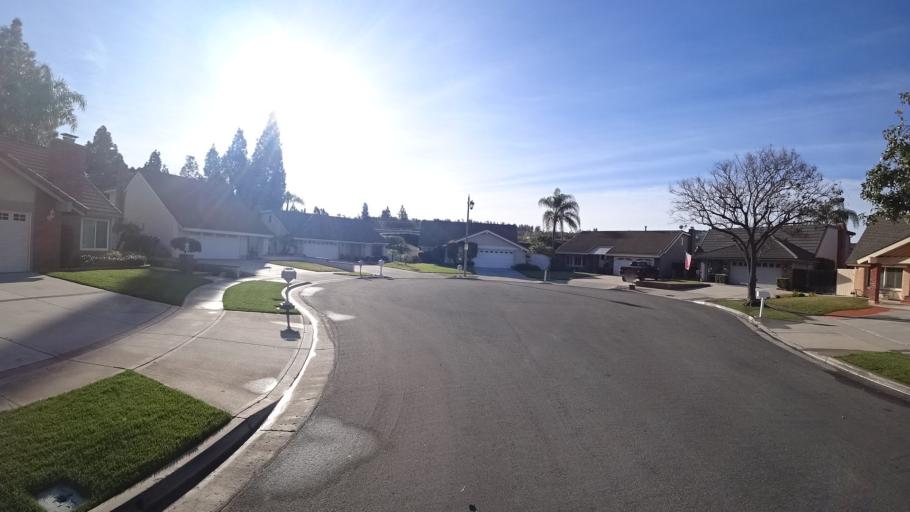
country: US
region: California
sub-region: Orange County
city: Yorba Linda
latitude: 33.8580
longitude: -117.7758
